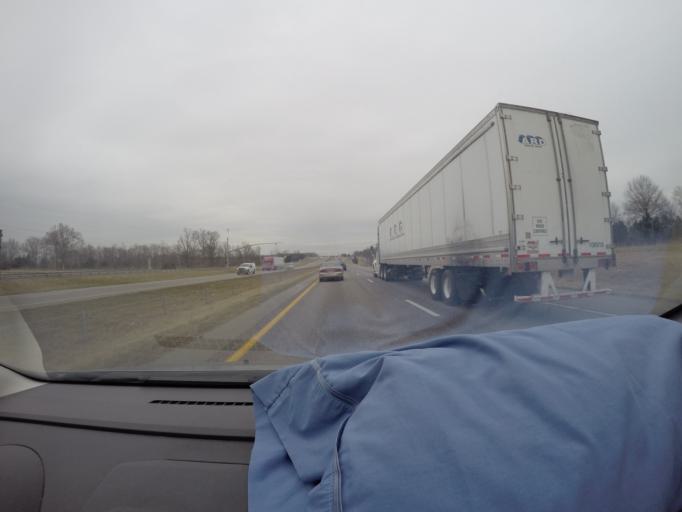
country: US
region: Missouri
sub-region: Saint Charles County
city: Wentzville
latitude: 38.8071
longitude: -90.9162
